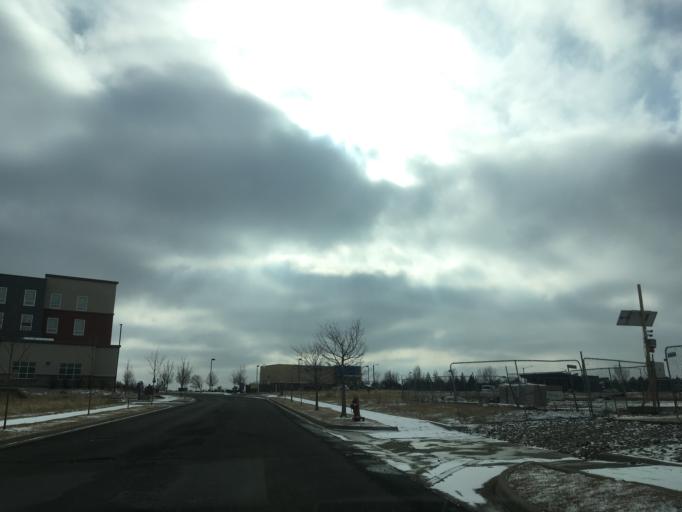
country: US
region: Colorado
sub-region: Boulder County
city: Lafayette
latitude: 39.9737
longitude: -105.0873
